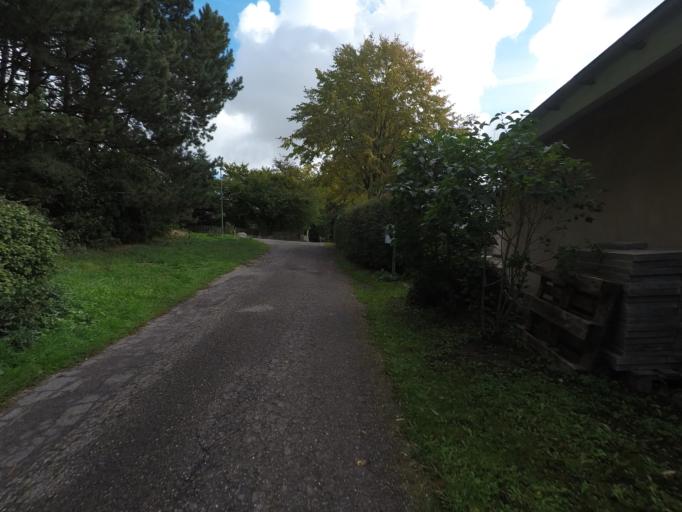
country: DK
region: Capital Region
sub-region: Egedal Kommune
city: Smorumnedre
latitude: 55.7385
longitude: 12.3163
